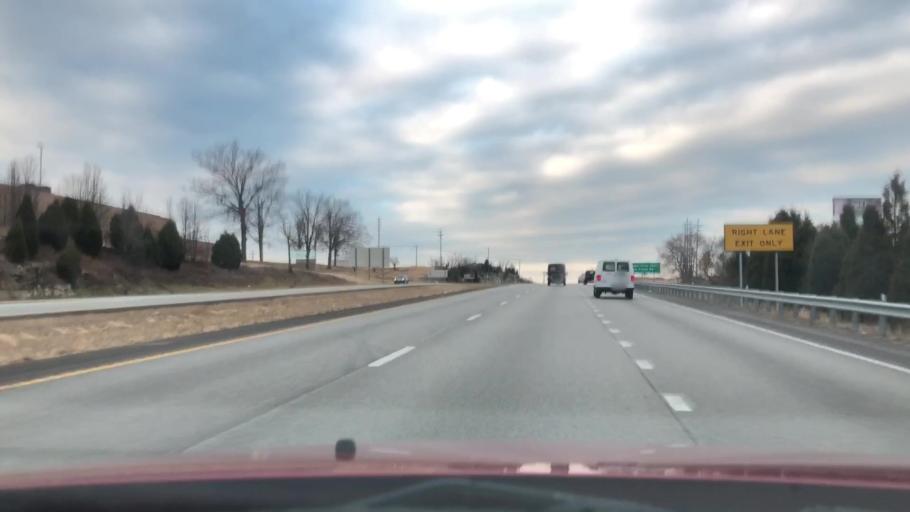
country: US
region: Missouri
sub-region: Taney County
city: Branson
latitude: 36.6604
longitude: -93.2220
